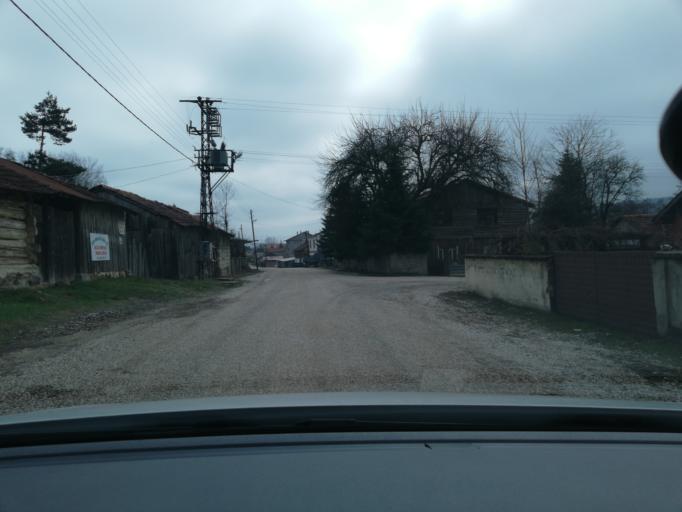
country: TR
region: Bolu
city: Bolu
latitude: 40.7164
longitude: 31.4745
